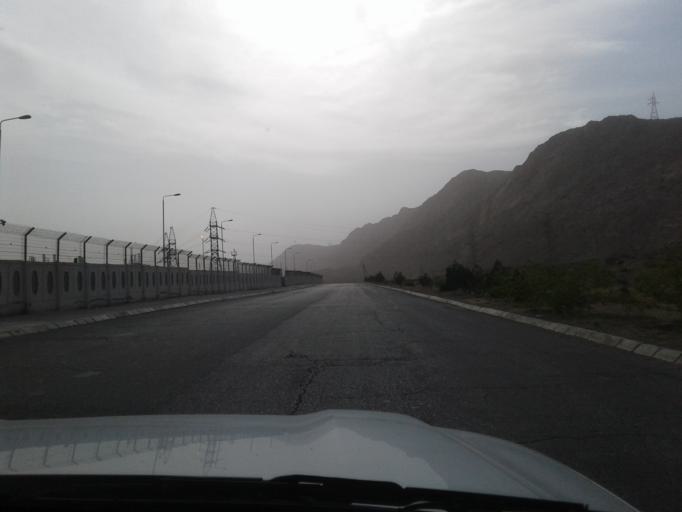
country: TM
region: Balkan
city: Turkmenbasy
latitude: 40.0339
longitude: 52.9614
